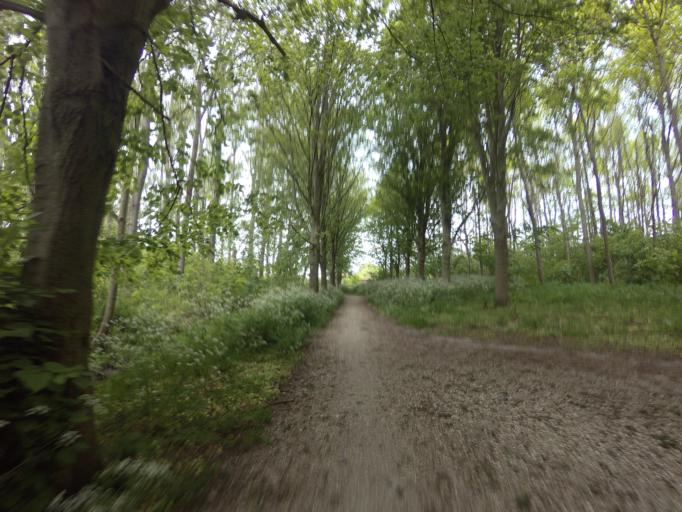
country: NL
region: Friesland
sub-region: Sudwest Fryslan
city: Bolsward
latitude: 53.0964
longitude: 5.4733
